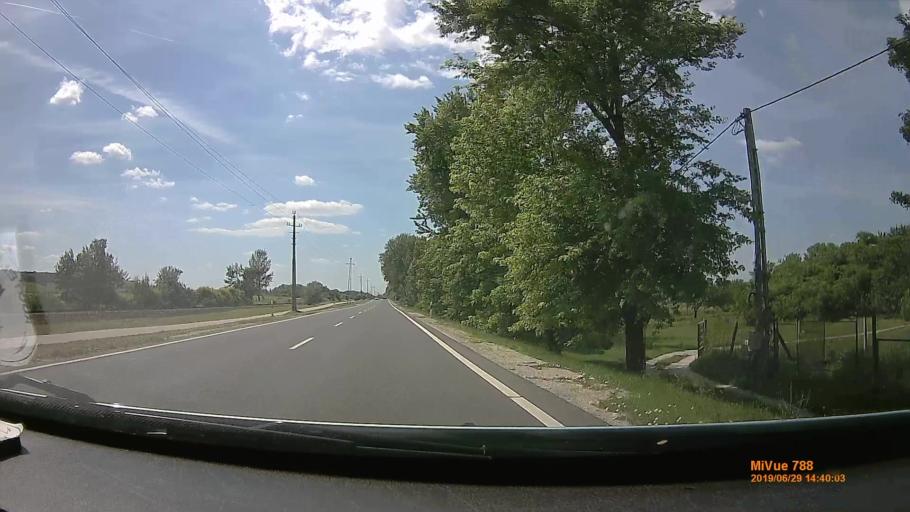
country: HU
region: Komarom-Esztergom
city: Nyergesujfalu
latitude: 47.7551
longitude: 18.5935
